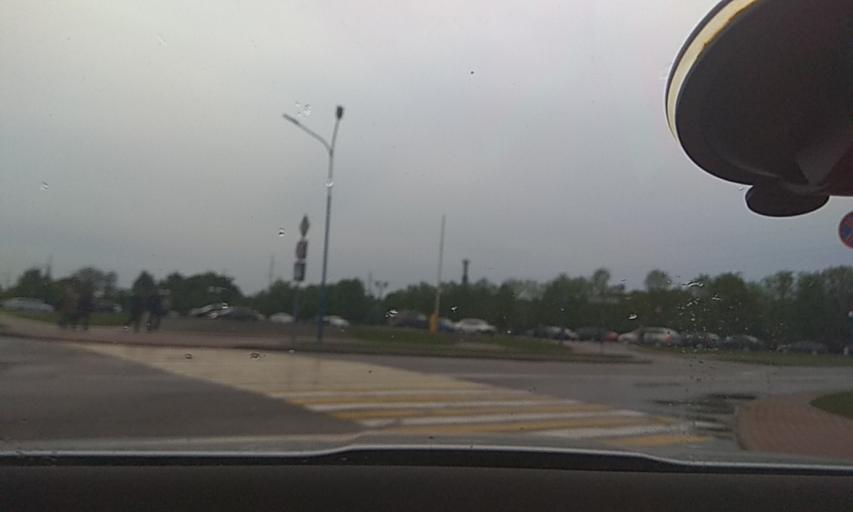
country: BY
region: Grodnenskaya
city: Hrodna
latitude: 53.6774
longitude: 23.8933
